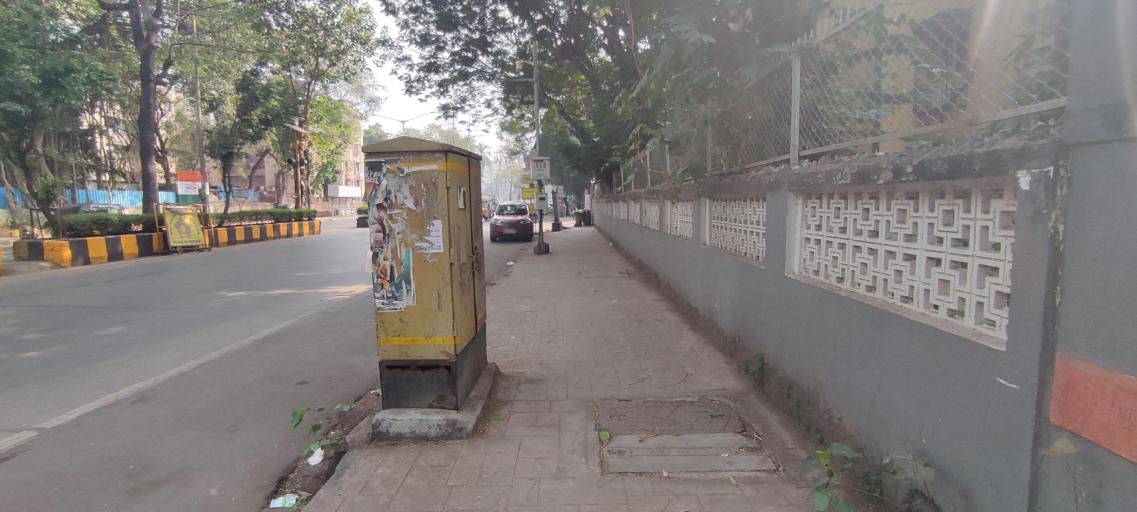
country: IN
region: Maharashtra
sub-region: Mumbai Suburban
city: Mumbai
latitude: 19.1186
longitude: 72.8284
